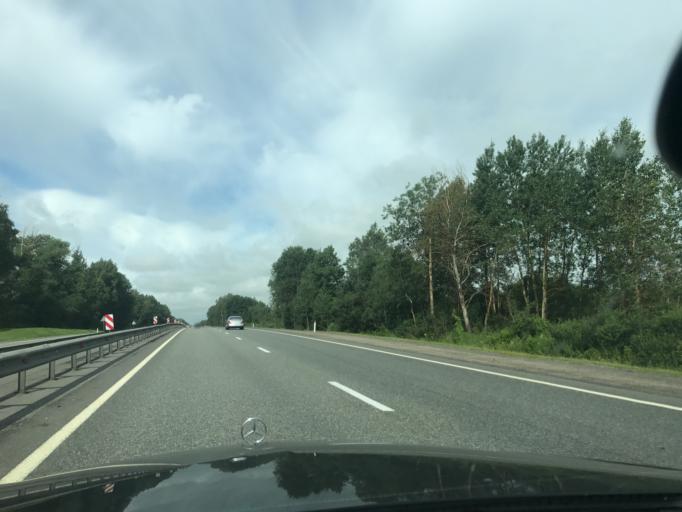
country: RU
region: Smolensk
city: Yartsevo
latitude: 55.0590
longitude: 32.5737
